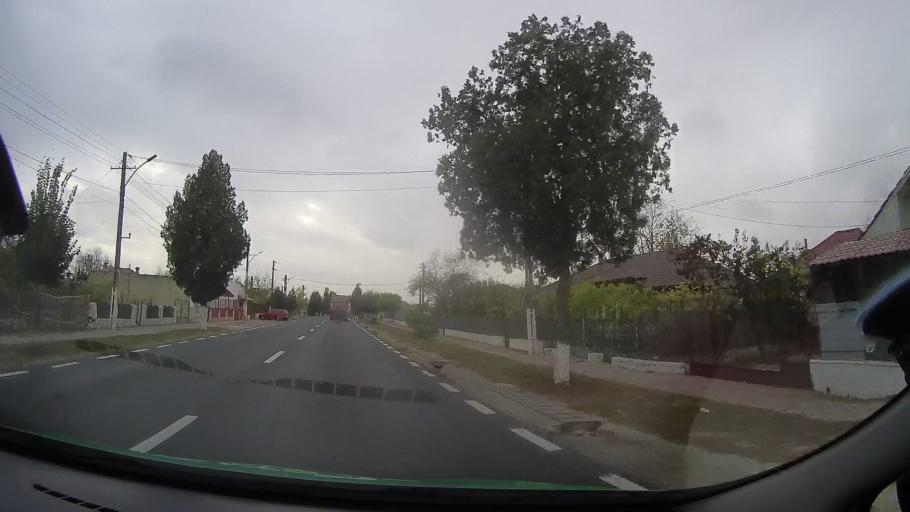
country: RO
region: Constanta
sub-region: Comuna Castelu
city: Castelu
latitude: 44.2547
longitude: 28.3353
